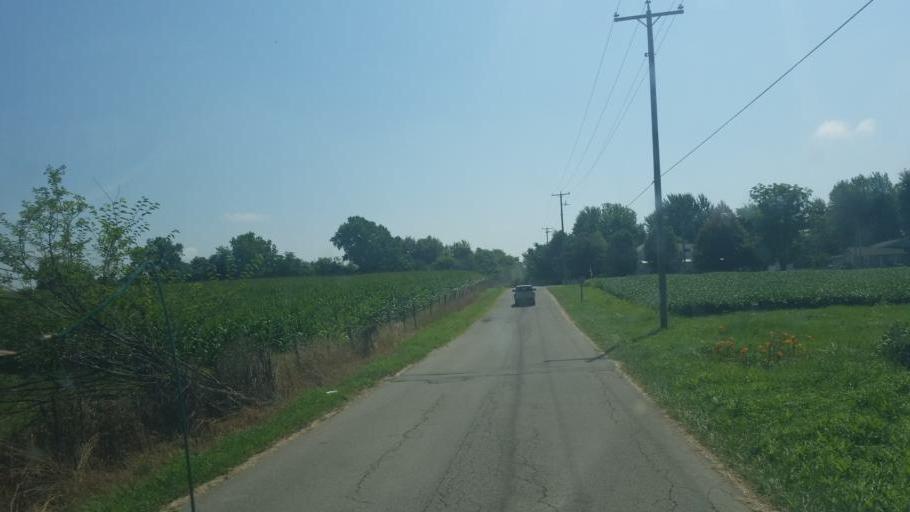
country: US
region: Ohio
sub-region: Hardin County
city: Kenton
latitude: 40.6598
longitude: -83.6142
